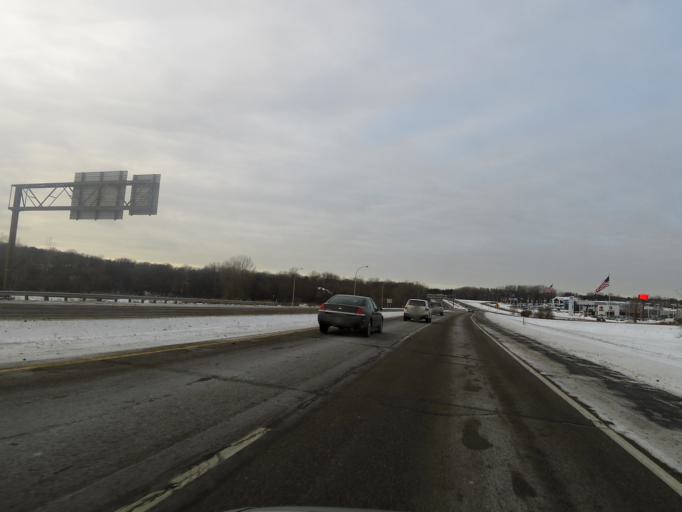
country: US
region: Minnesota
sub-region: Dakota County
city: West Saint Paul
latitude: 44.8783
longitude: -93.0825
